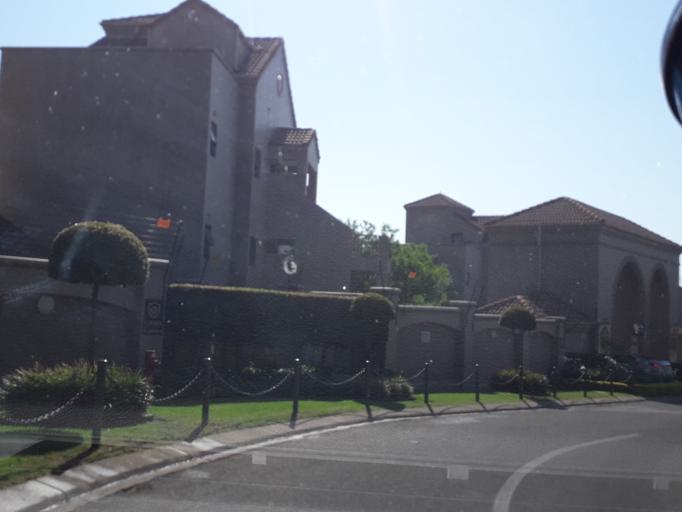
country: ZA
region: Gauteng
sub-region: City of Johannesburg Metropolitan Municipality
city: Midrand
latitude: -26.0343
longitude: 28.0520
